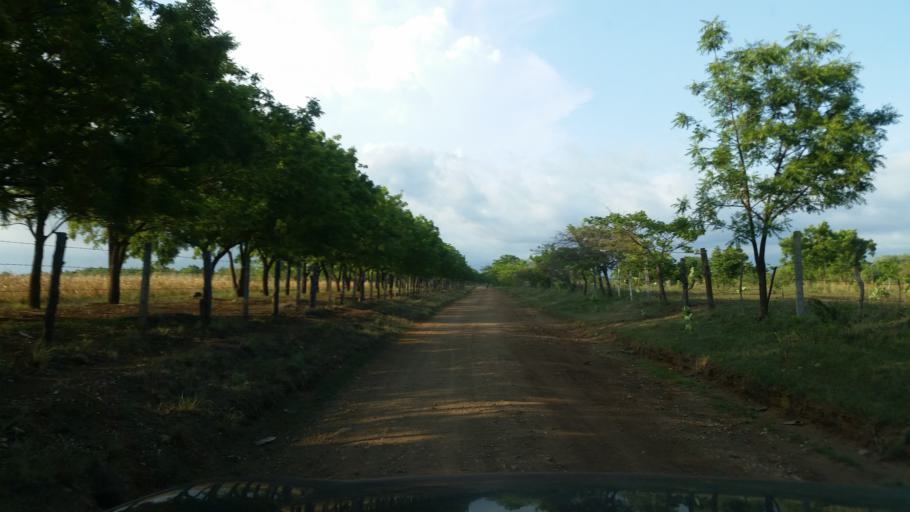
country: NI
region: Managua
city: Masachapa
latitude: 11.7610
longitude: -86.4898
